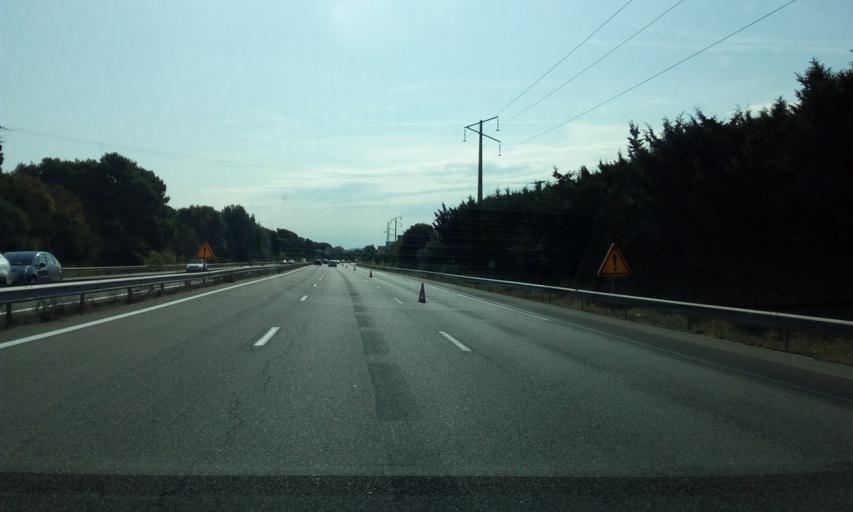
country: FR
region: Provence-Alpes-Cote d'Azur
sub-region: Departement du Var
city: Sanary-sur-Mer
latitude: 43.1284
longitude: 5.8190
